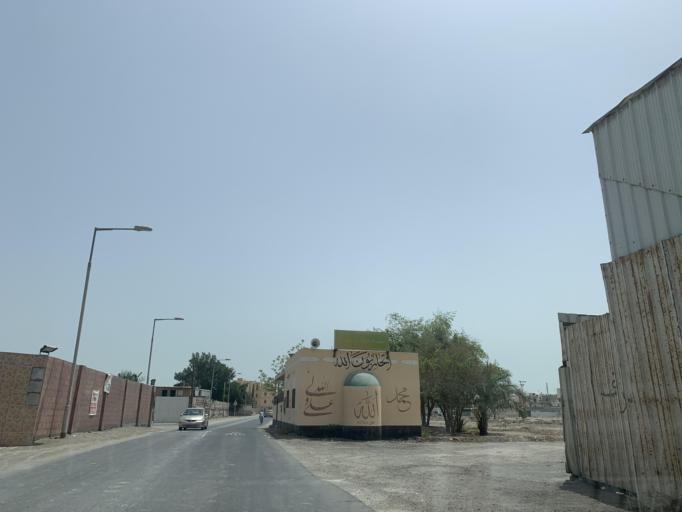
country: BH
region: Northern
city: Sitrah
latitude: 26.1348
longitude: 50.5935
